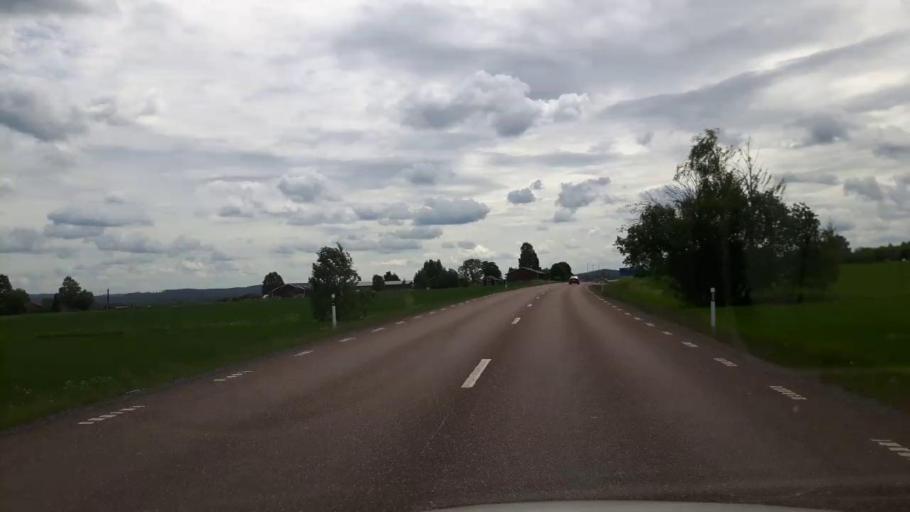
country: SE
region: Dalarna
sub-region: Hedemora Kommun
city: Hedemora
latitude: 60.3020
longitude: 15.9778
